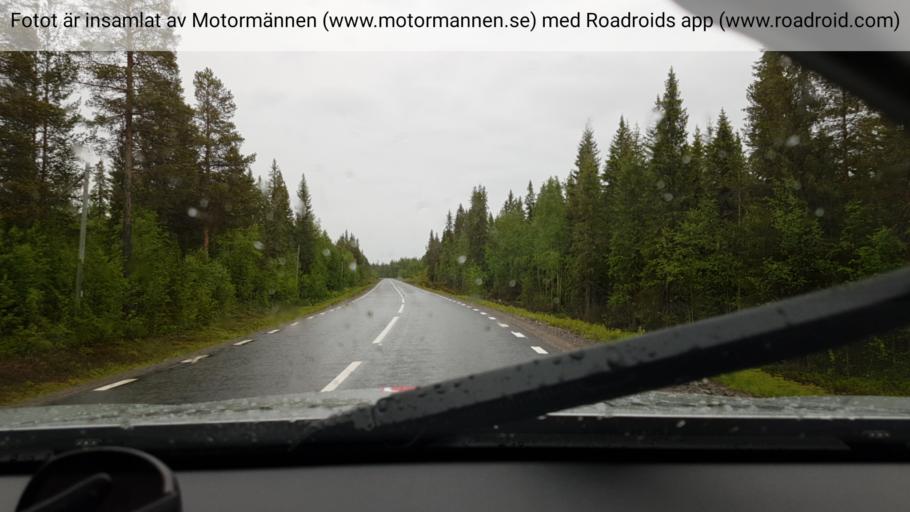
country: SE
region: Vaesterbotten
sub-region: Sorsele Kommun
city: Sorsele
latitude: 65.7770
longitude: 17.0141
